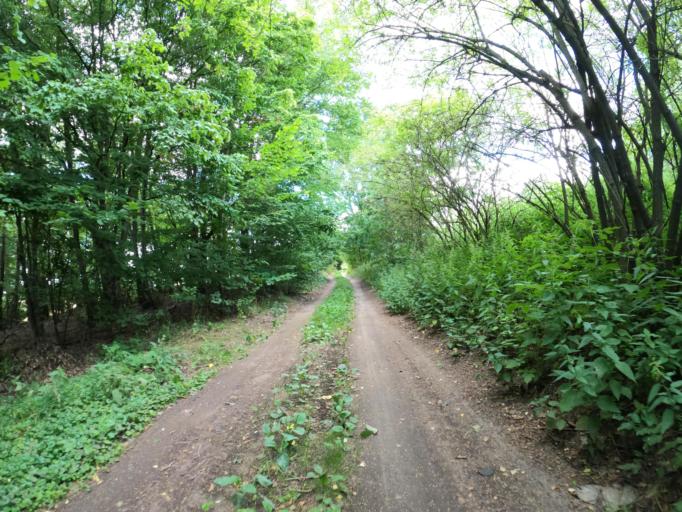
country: PL
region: West Pomeranian Voivodeship
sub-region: Powiat swidwinski
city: Swidwin
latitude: 53.7520
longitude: 15.8189
